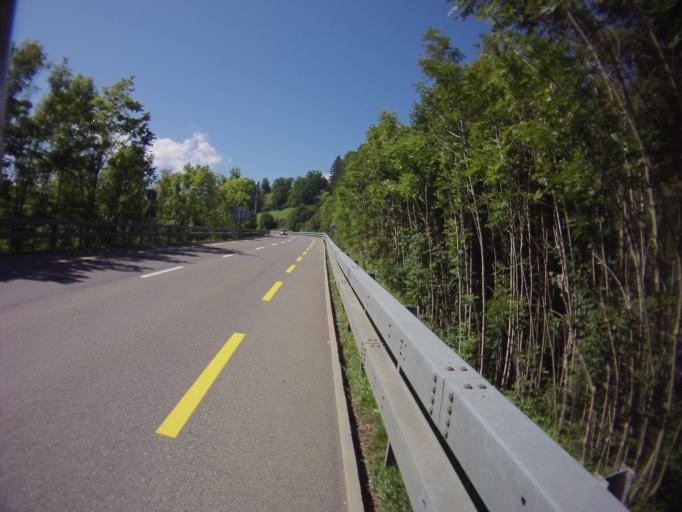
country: CH
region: Schwyz
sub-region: Bezirk Einsiedeln
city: Einsiedeln
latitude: 47.1454
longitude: 8.7503
